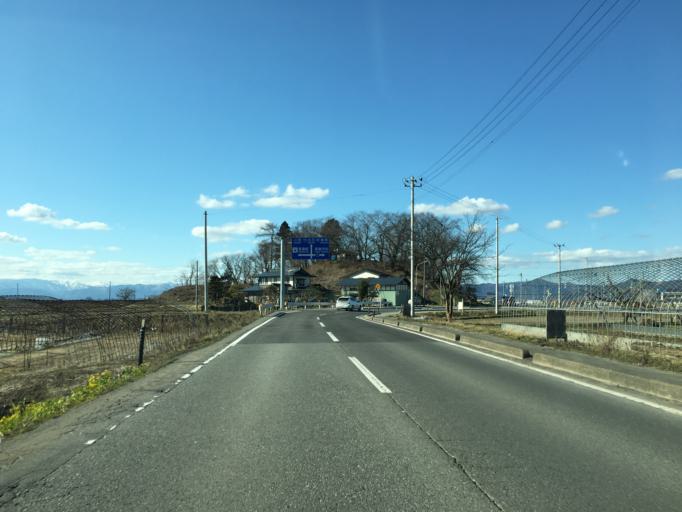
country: JP
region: Yamagata
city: Takahata
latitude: 37.9923
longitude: 140.1792
